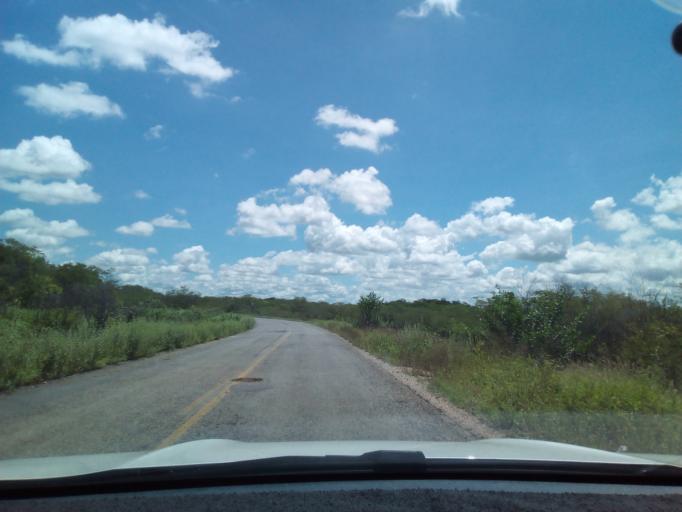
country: BR
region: Rio Grande do Norte
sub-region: Caico
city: Caico
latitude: -6.4322
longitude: -37.2072
